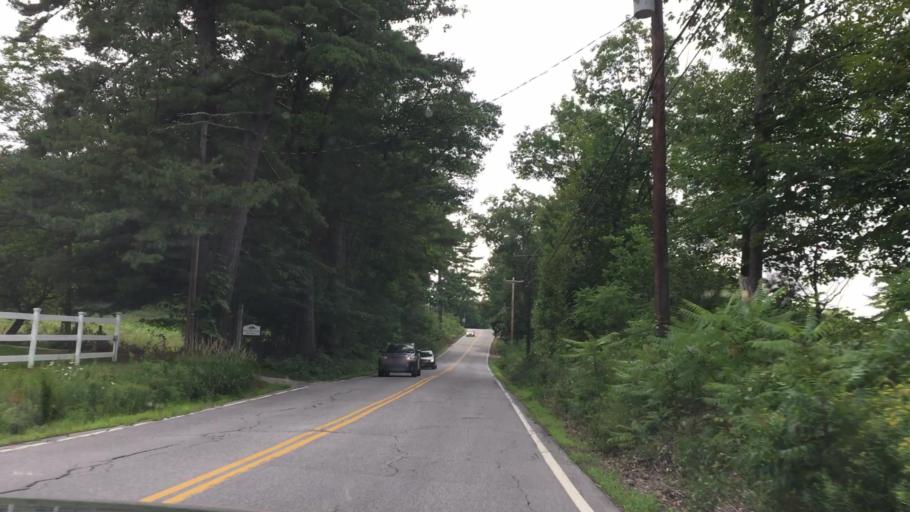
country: US
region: New Hampshire
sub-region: Carroll County
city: Center Harbor
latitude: 43.7119
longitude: -71.4693
